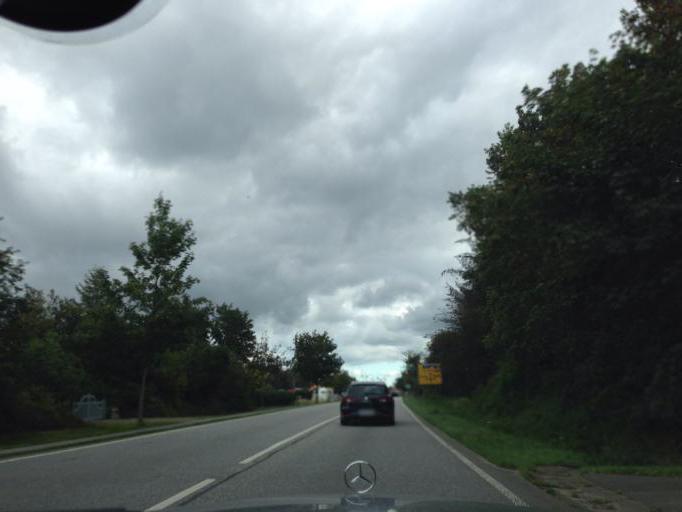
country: DE
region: Schleswig-Holstein
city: Stadum
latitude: 54.7429
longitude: 9.0492
